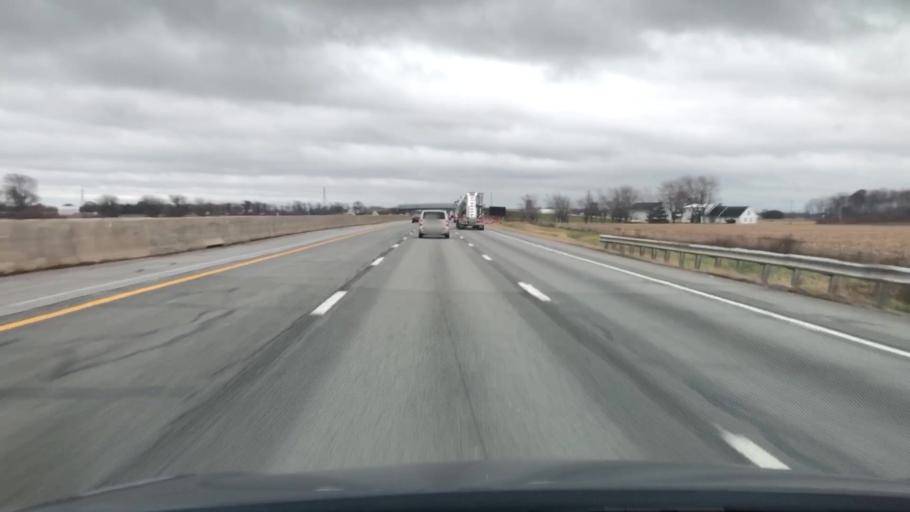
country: US
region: Ohio
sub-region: Sandusky County
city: Stony Prairie
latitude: 41.4172
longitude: -83.1571
